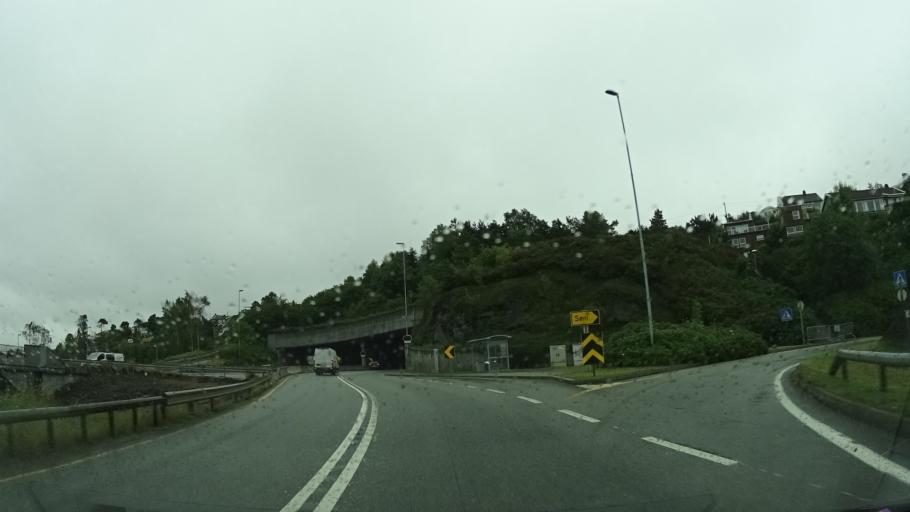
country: NO
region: Vest-Agder
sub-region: Kristiansand
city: Justvik
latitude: 58.1606
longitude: 8.0607
